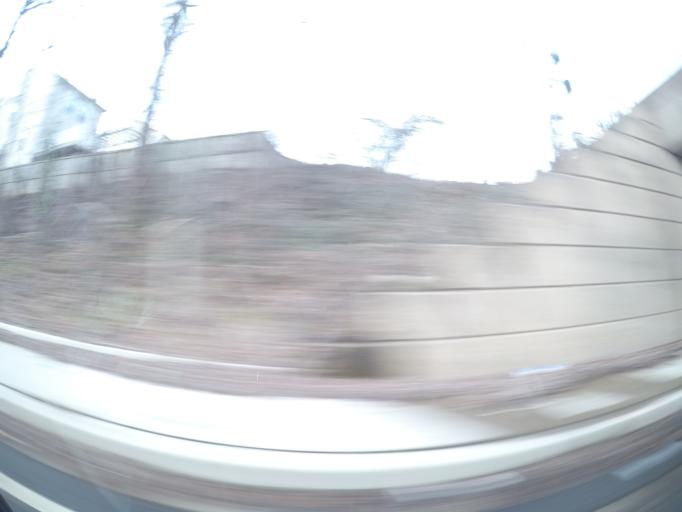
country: US
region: Maryland
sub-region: Howard County
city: Hanover
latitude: 39.1784
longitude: -76.7476
